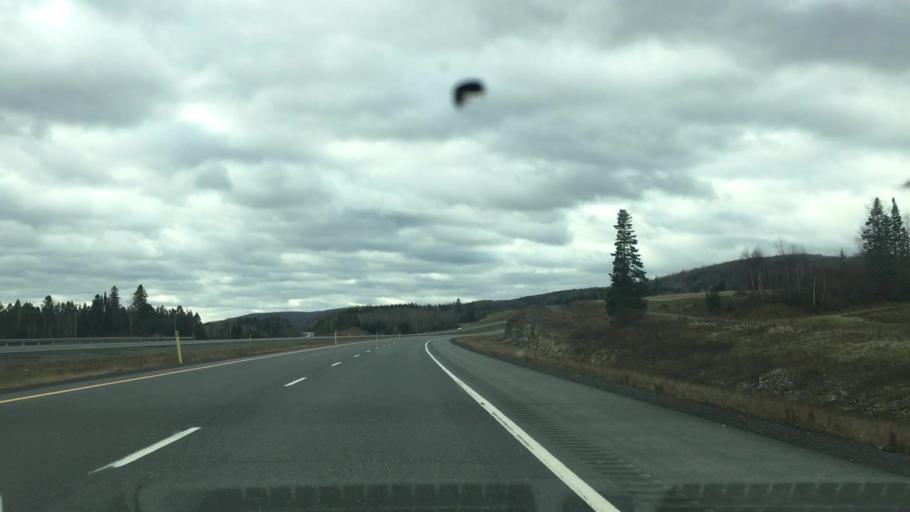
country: US
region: Maine
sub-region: Aroostook County
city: Fort Fairfield
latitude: 46.7369
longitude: -67.7177
